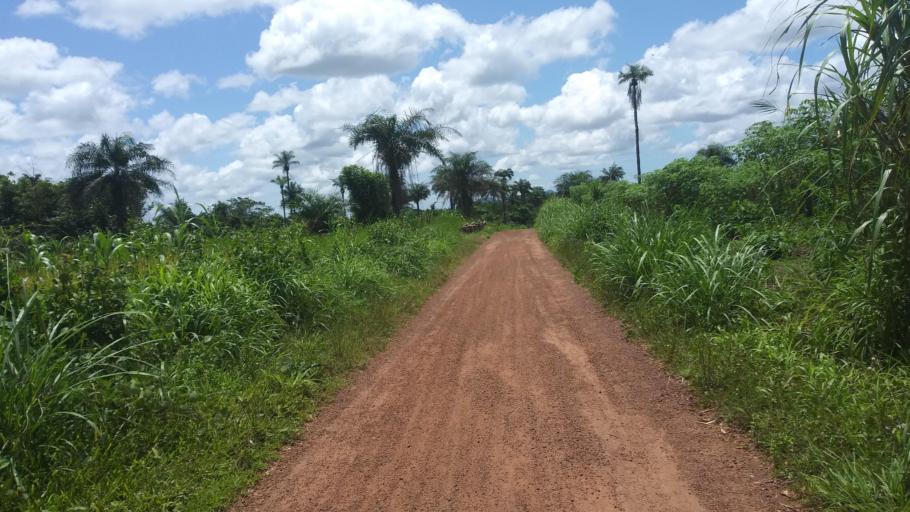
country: SL
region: Northern Province
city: Binkolo
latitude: 8.8795
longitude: -11.9610
